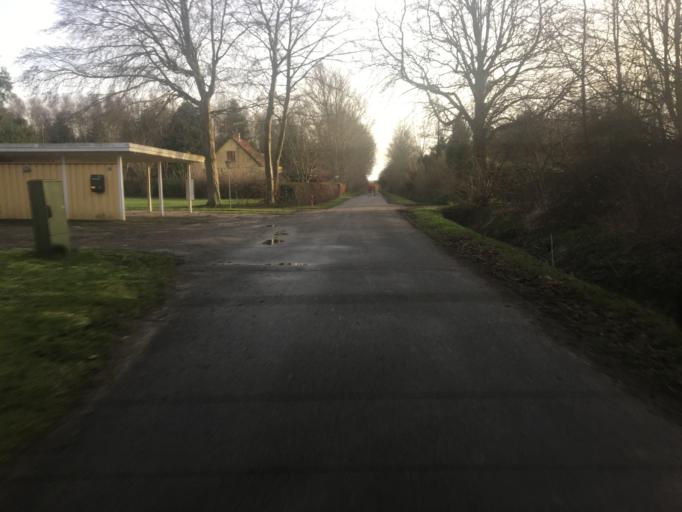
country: DK
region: Capital Region
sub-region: Tarnby Kommune
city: Tarnby
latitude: 55.5687
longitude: 12.5951
